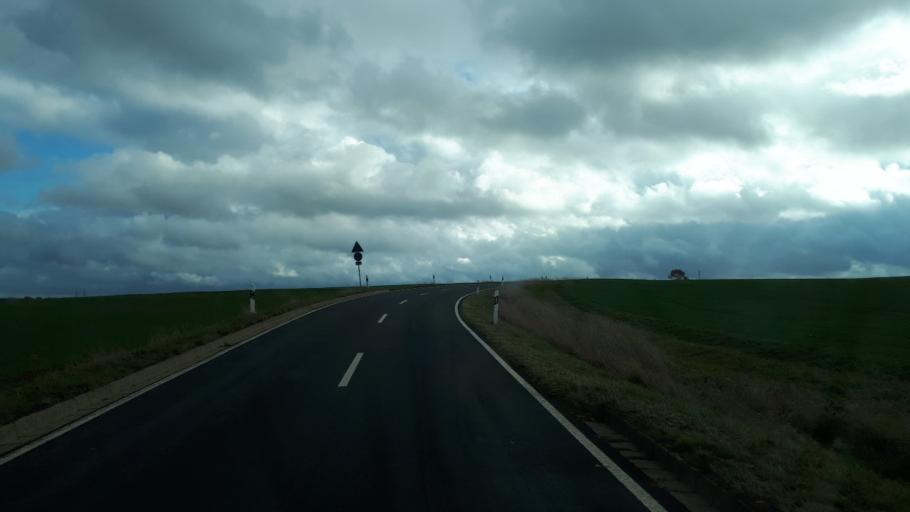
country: DE
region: Rheinland-Pfalz
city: Wirfus
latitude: 50.2059
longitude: 7.2003
